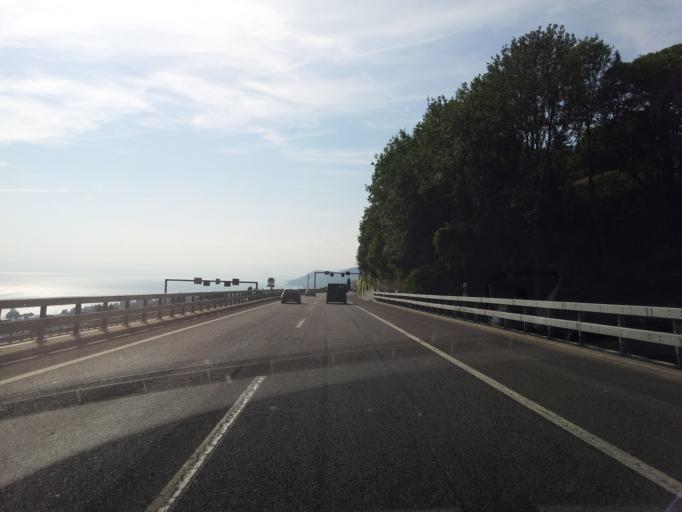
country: CH
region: Vaud
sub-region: Riviera-Pays-d'Enhaut District
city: Montreux
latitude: 46.4417
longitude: 6.9124
